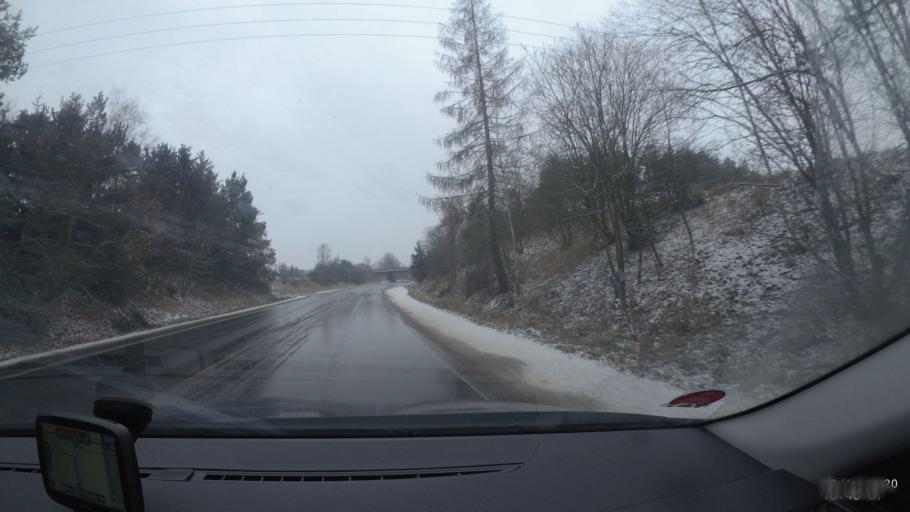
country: CZ
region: Central Bohemia
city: Nove Straseci
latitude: 50.1638
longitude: 13.8983
